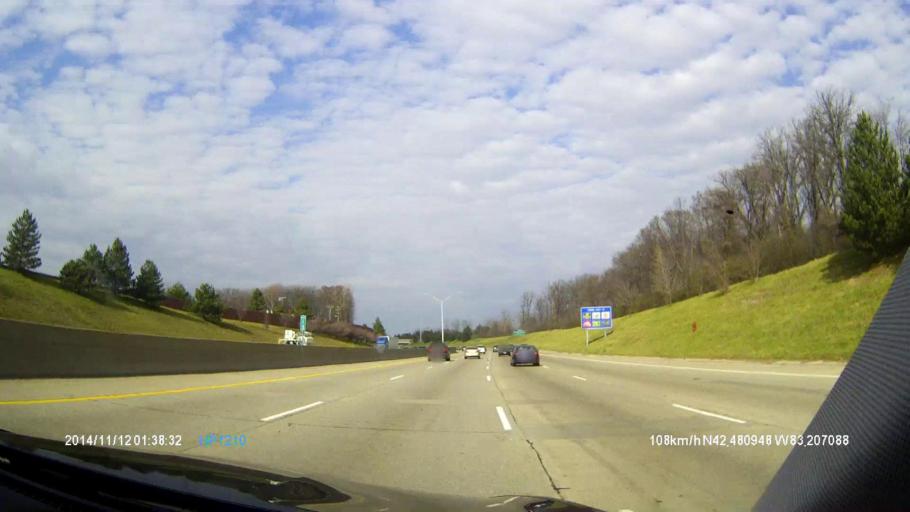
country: US
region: Michigan
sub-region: Oakland County
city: Southfield
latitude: 42.4812
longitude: -83.2071
